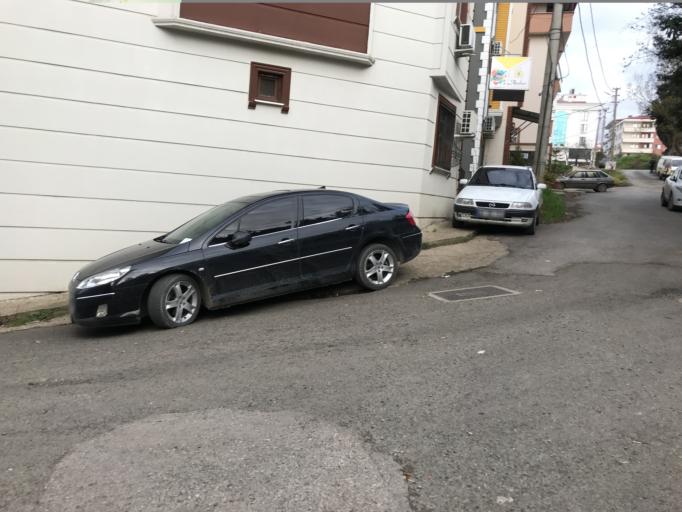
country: TR
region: Trabzon
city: Trabzon
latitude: 40.9905
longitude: 39.7770
